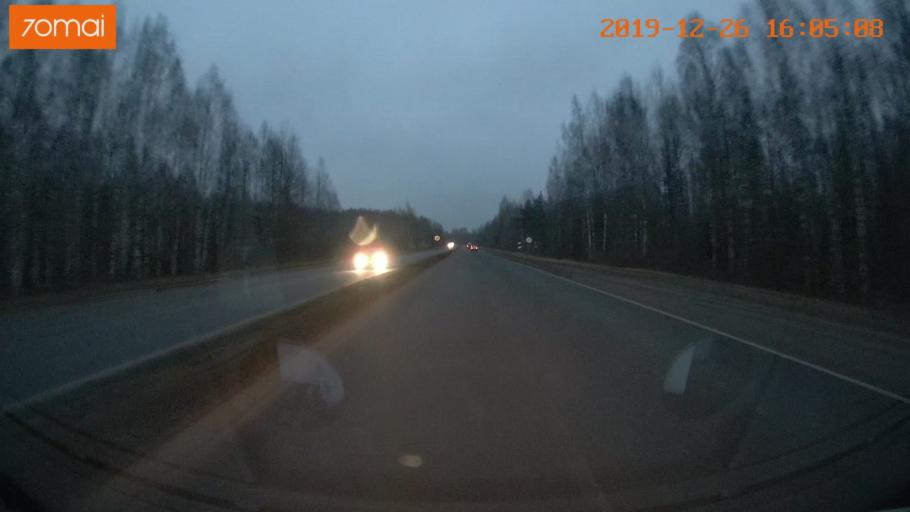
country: RU
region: Jaroslavl
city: Rybinsk
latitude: 58.0069
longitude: 38.8879
